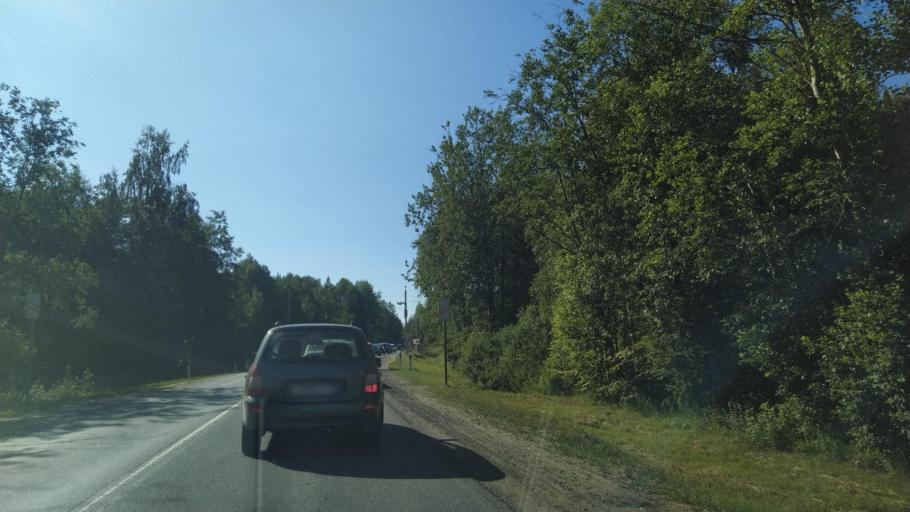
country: RU
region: Leningrad
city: Kirovsk
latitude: 59.9258
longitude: 30.9665
